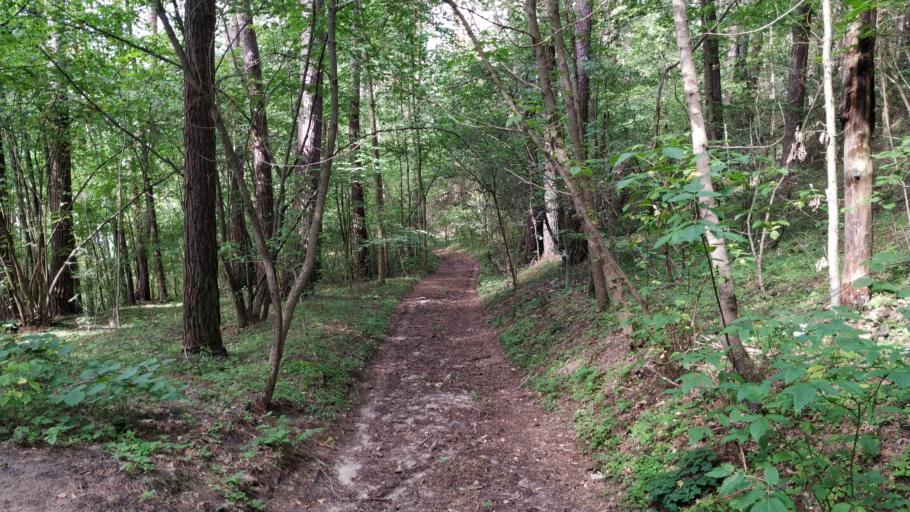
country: LT
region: Vilnius County
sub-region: Vilniaus Rajonas
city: Vievis
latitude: 54.8094
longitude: 24.9658
